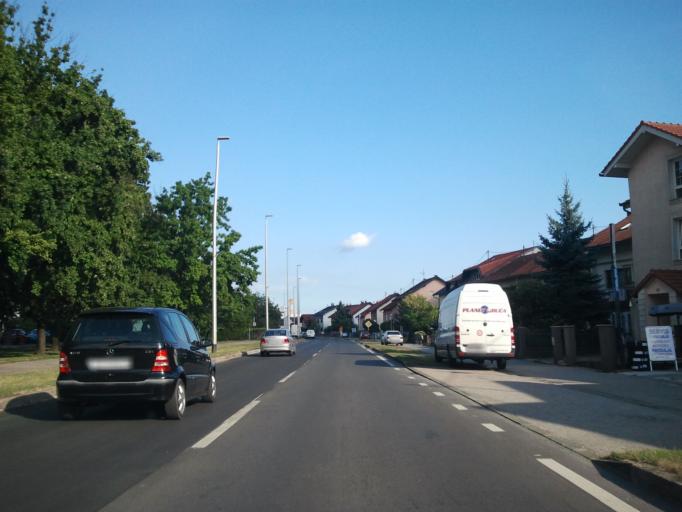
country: HR
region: Zagrebacka
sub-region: Grad Velika Gorica
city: Velika Gorica
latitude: 45.7164
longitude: 16.0586
